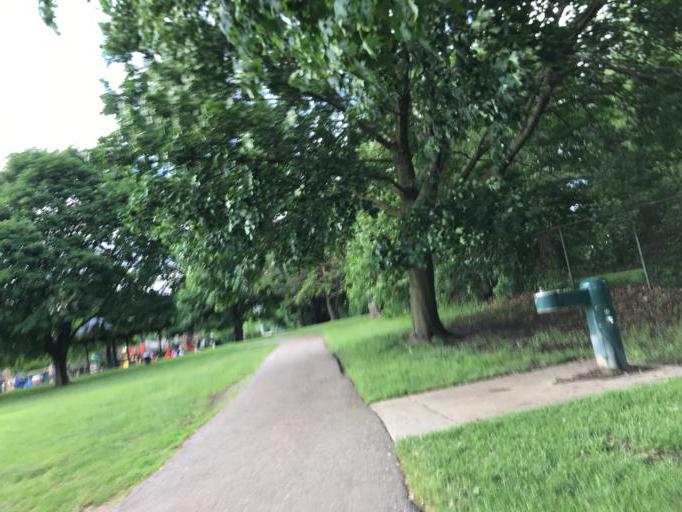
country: US
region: Michigan
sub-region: Oakland County
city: South Lyon
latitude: 42.4556
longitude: -83.6528
